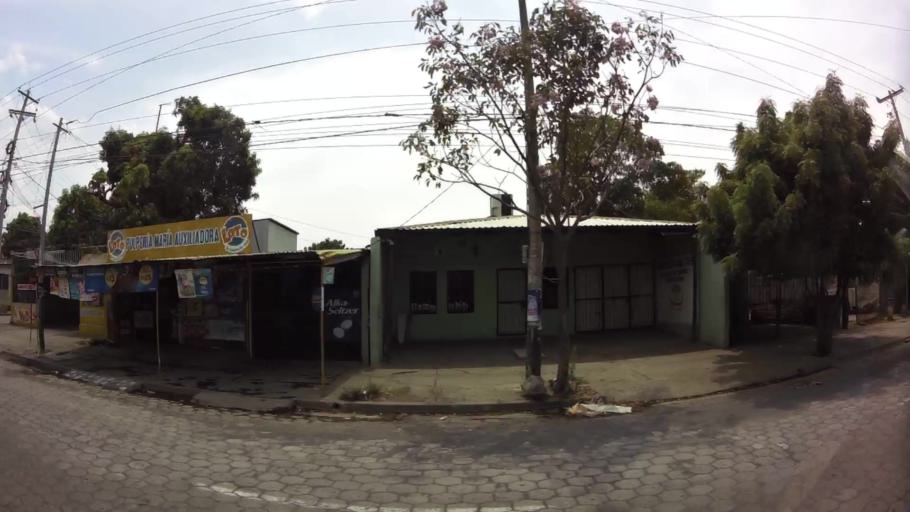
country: NI
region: Managua
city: Ciudad Sandino
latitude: 12.1468
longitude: -86.3048
